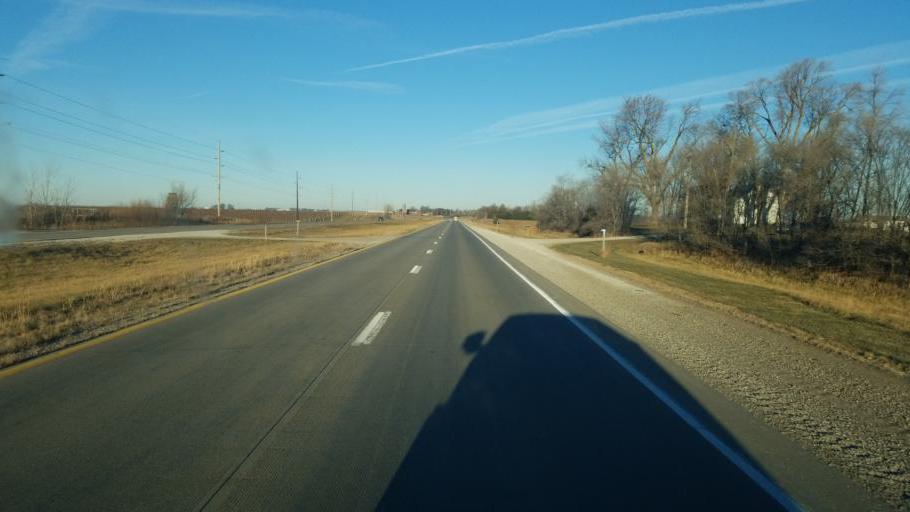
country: US
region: Iowa
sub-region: Mahaska County
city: Oskaloosa
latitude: 41.3422
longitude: -92.7410
